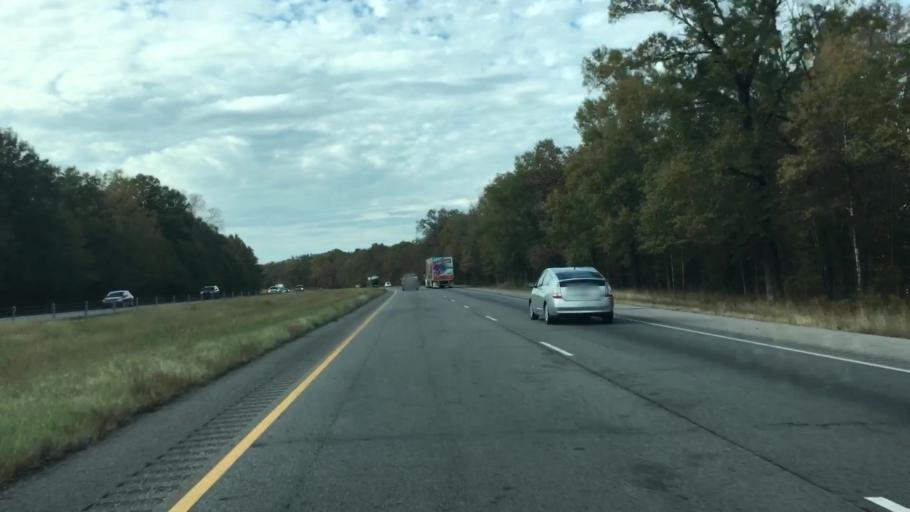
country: US
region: Arkansas
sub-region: Pope County
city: Atkins
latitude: 35.2434
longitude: -92.8622
